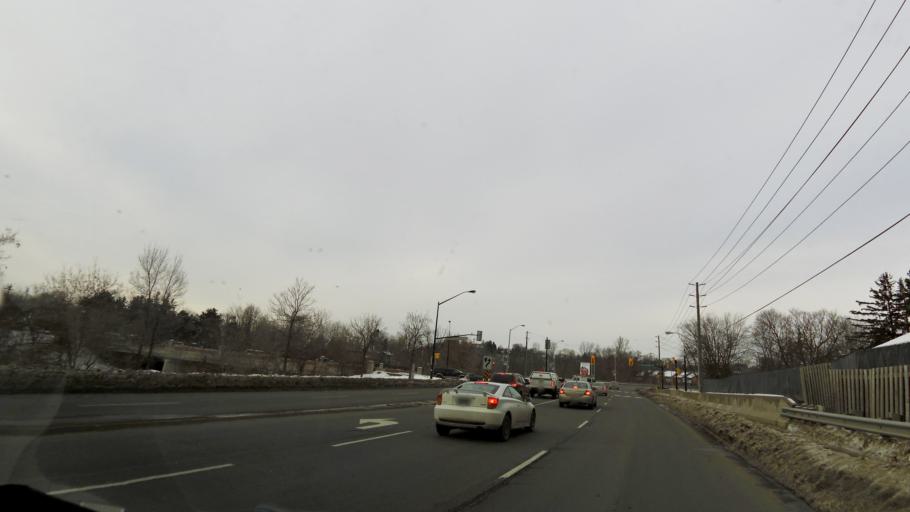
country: CA
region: Ontario
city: Vaughan
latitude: 43.7859
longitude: -79.5887
